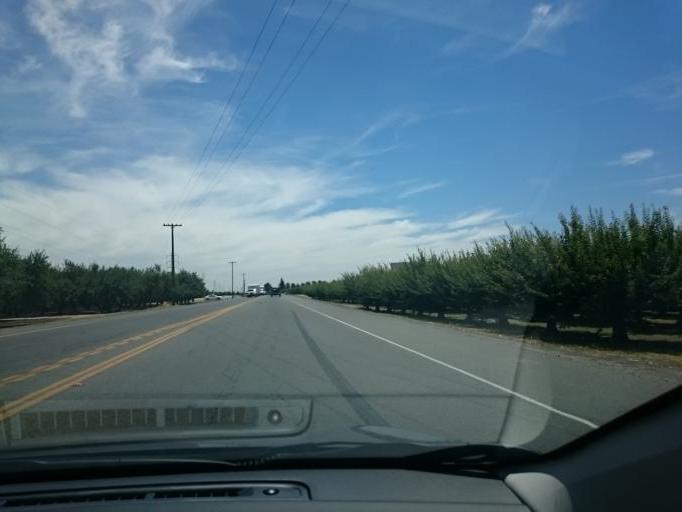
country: US
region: California
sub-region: Stanislaus County
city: Hughson
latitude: 37.6367
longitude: -120.8478
